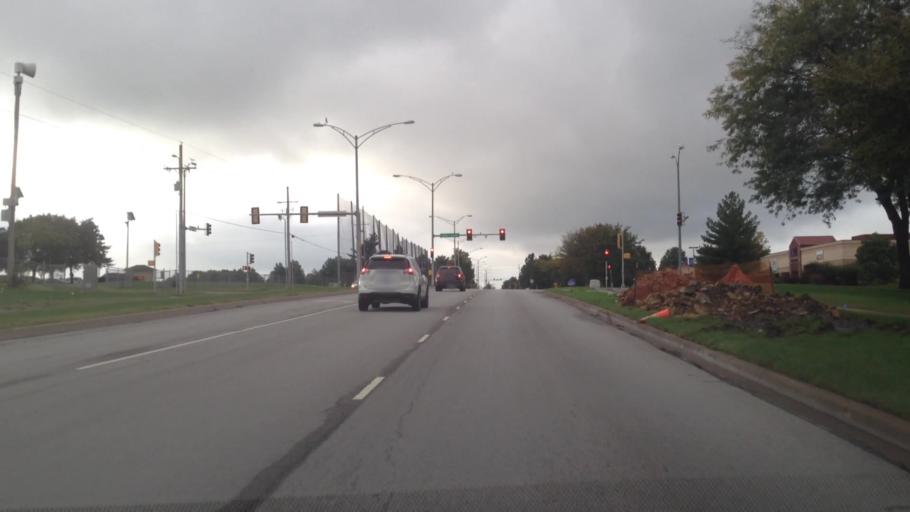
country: US
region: Kansas
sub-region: Johnson County
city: Lenexa
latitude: 38.9025
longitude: -94.7238
